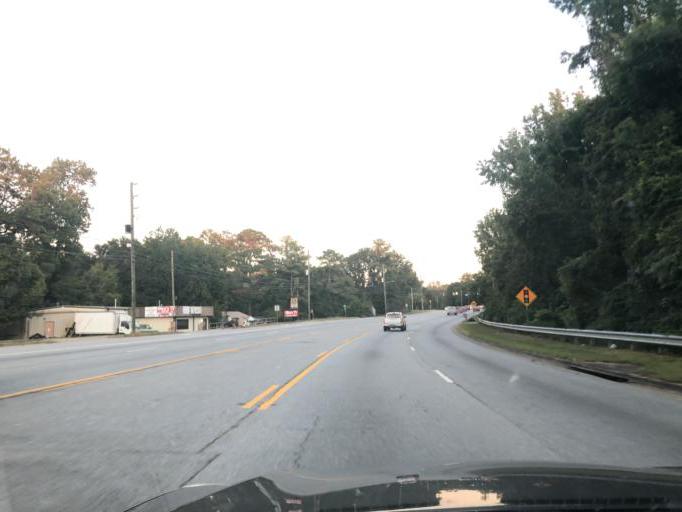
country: US
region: Georgia
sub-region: Muscogee County
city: Columbus
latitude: 32.4669
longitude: -84.9030
